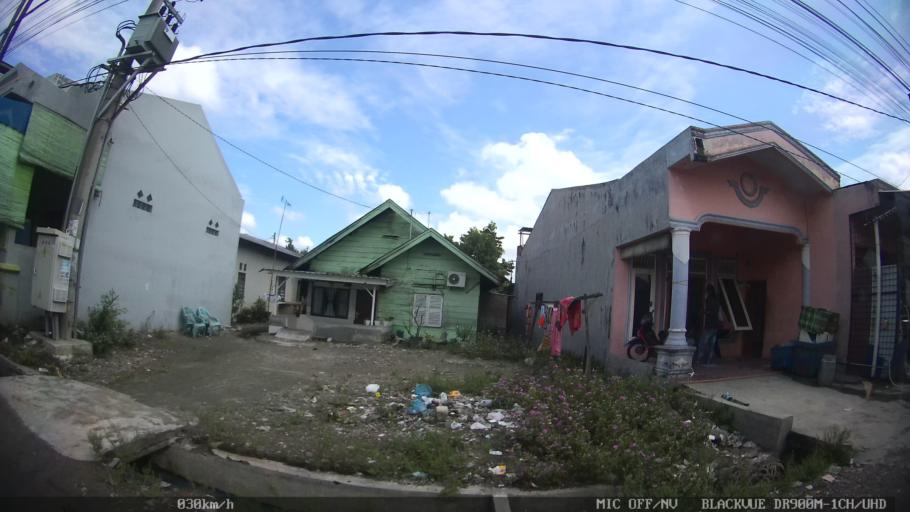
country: ID
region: North Sumatra
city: Medan
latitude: 3.6021
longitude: 98.7650
